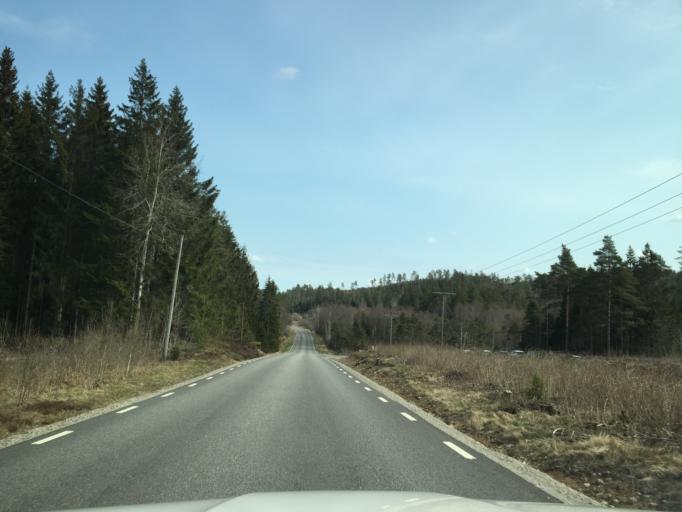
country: SE
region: Vaestra Goetaland
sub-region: Lilla Edets Kommun
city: Lodose
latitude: 58.0760
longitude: 12.0295
